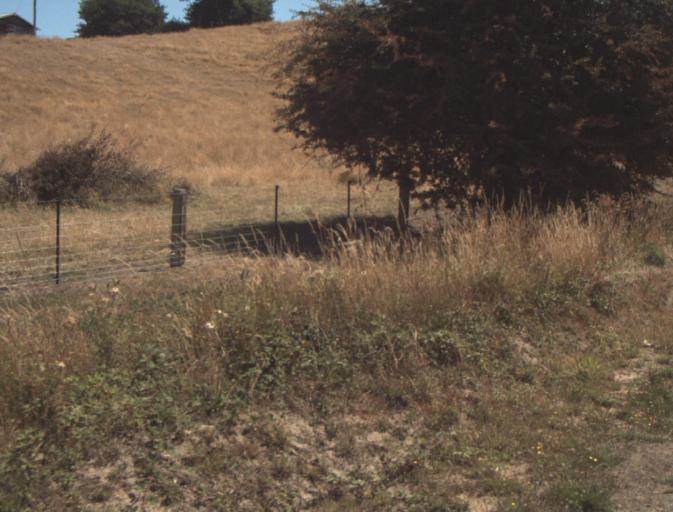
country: AU
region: Tasmania
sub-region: Launceston
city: Mayfield
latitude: -41.2520
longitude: 147.1338
